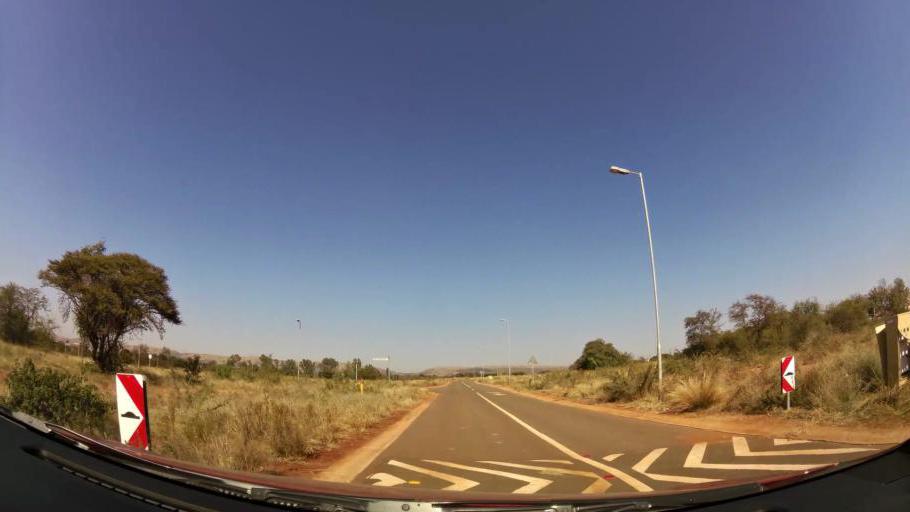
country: ZA
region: North-West
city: Ga-Rankuwa
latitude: -25.6423
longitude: 28.0802
